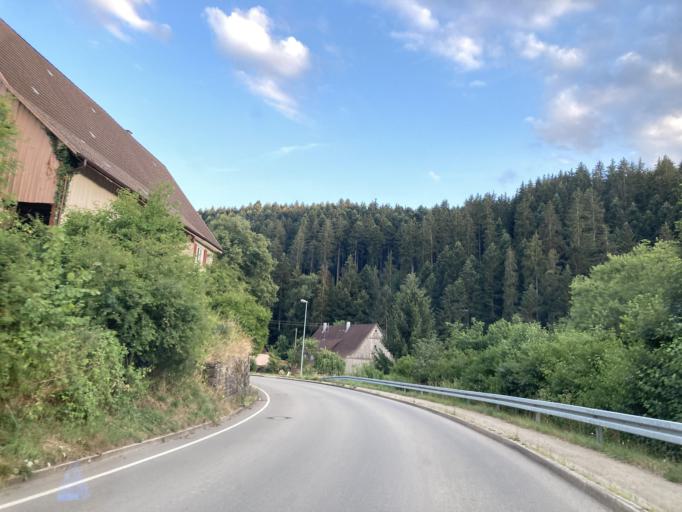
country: DE
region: Baden-Wuerttemberg
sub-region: Karlsruhe Region
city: Glatten
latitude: 48.4176
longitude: 8.5265
